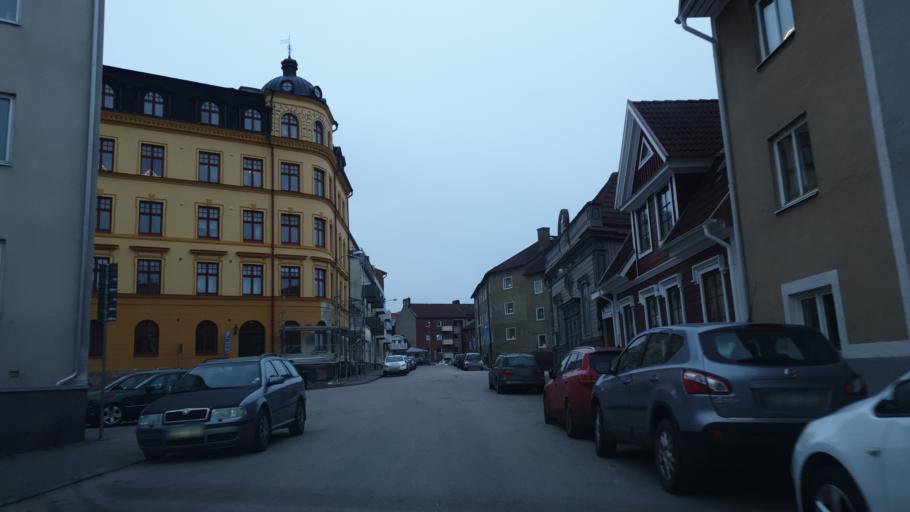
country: SE
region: Blekinge
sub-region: Karlskrona Kommun
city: Karlskrona
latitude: 56.1609
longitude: 15.5782
